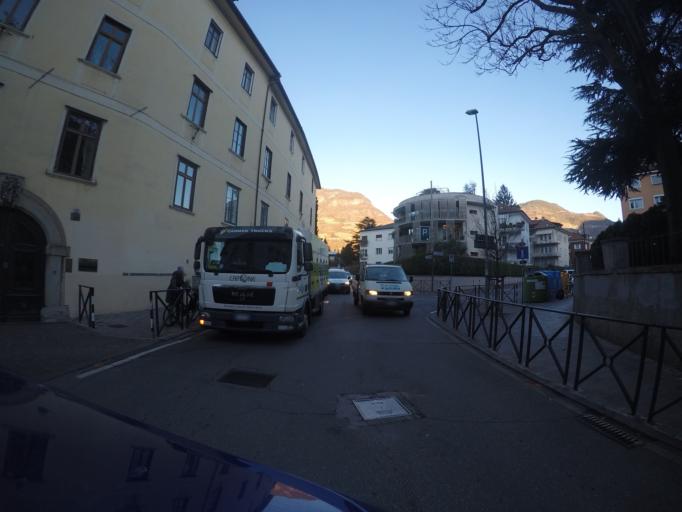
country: IT
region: Trentino-Alto Adige
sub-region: Bolzano
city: Bolzano
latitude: 46.5013
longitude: 11.3514
